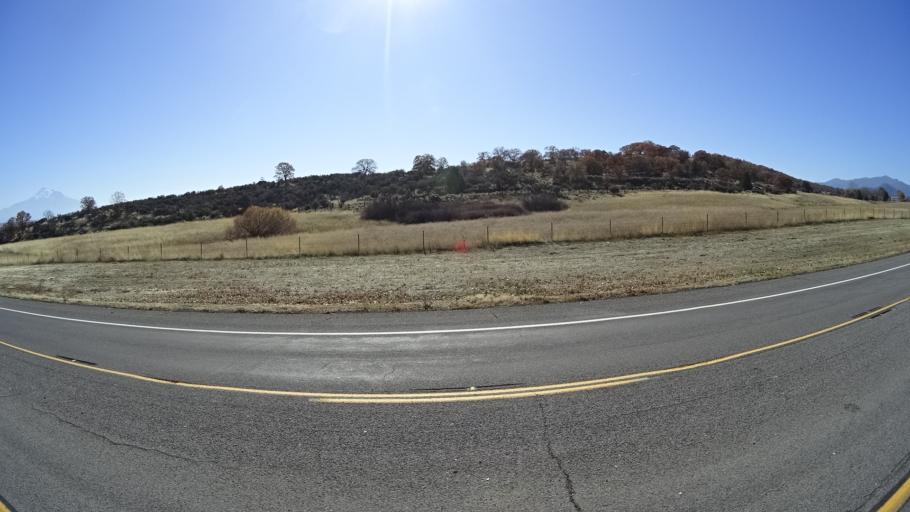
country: US
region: California
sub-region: Siskiyou County
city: Yreka
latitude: 41.7421
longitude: -122.6016
